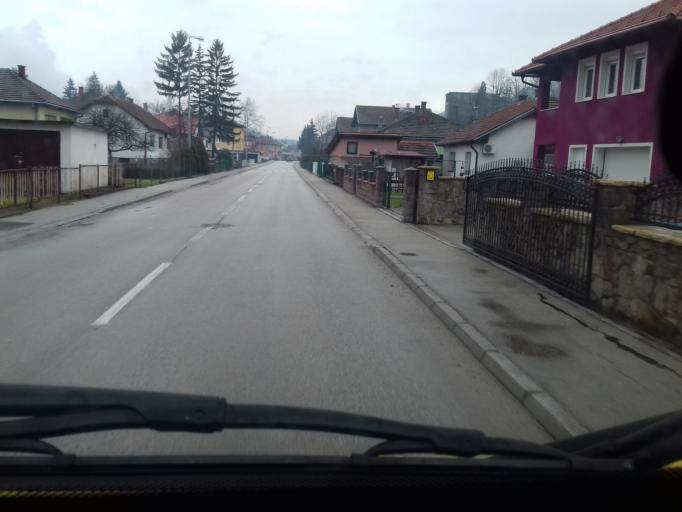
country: BA
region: Federation of Bosnia and Herzegovina
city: Maglaj
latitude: 44.5513
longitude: 18.0965
